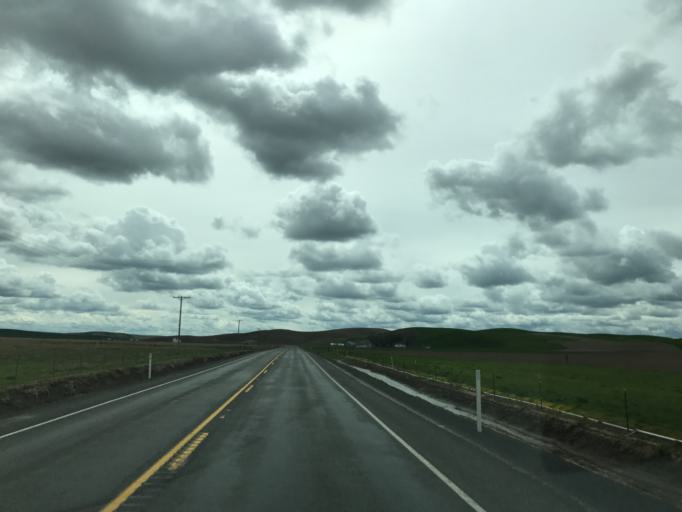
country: US
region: Washington
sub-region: Garfield County
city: Pomeroy
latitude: 46.7887
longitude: -117.6943
